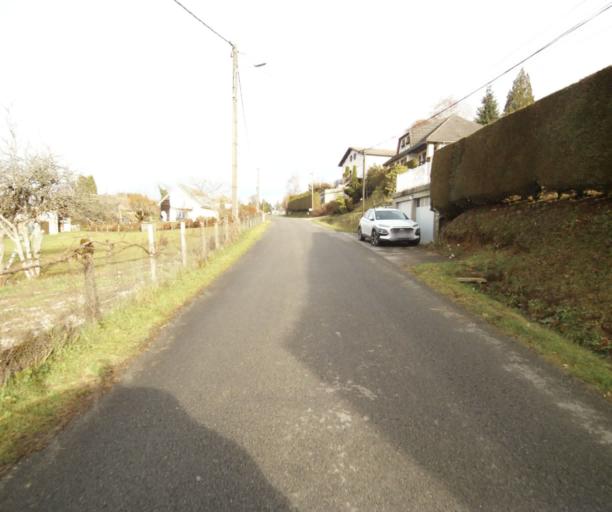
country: FR
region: Limousin
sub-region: Departement de la Correze
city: Saint-Mexant
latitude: 45.2688
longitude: 1.6801
